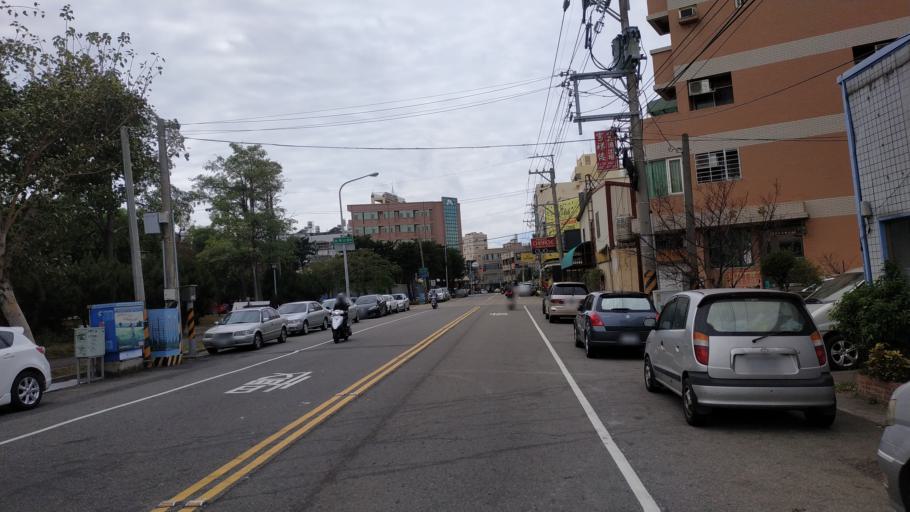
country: TW
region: Taiwan
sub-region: Taichung City
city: Taichung
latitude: 24.2298
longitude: 120.5701
